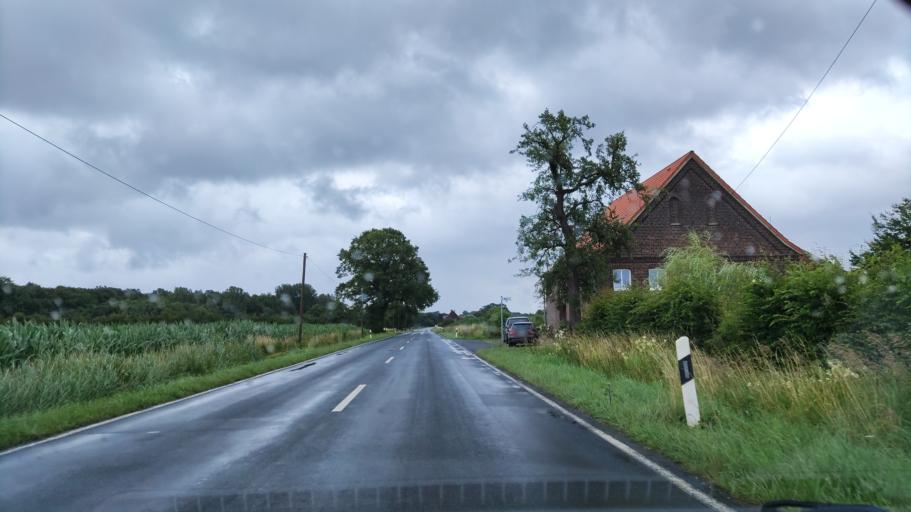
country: DE
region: North Rhine-Westphalia
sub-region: Regierungsbezirk Munster
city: Telgte
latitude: 51.8963
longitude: 7.7478
